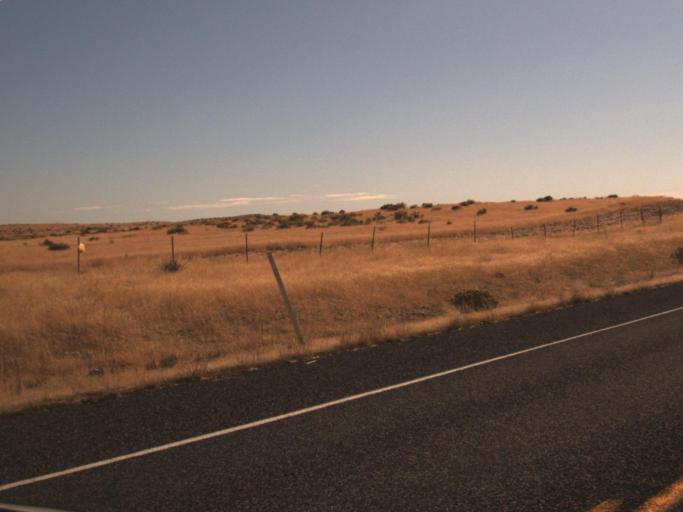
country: US
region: Washington
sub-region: Benton County
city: West Richland
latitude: 46.3928
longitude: -119.4382
